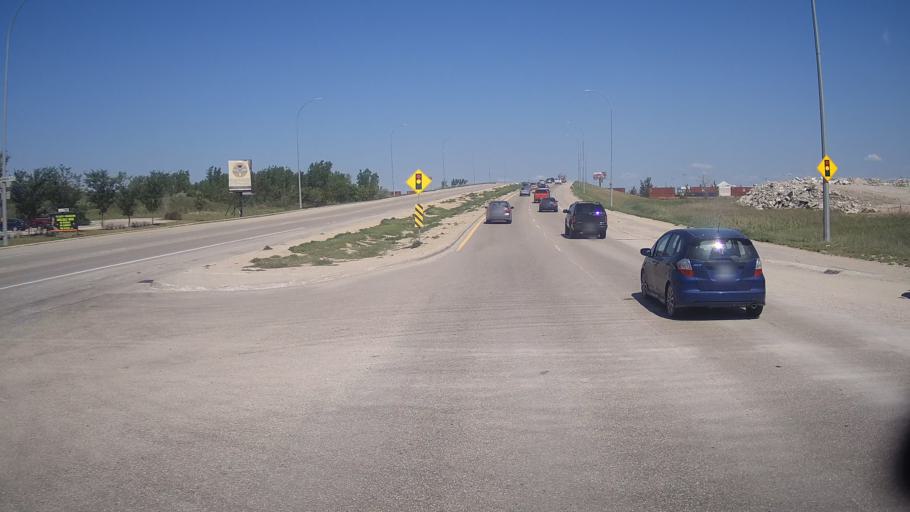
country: CA
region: Manitoba
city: Winnipeg
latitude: 49.8908
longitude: -97.0719
